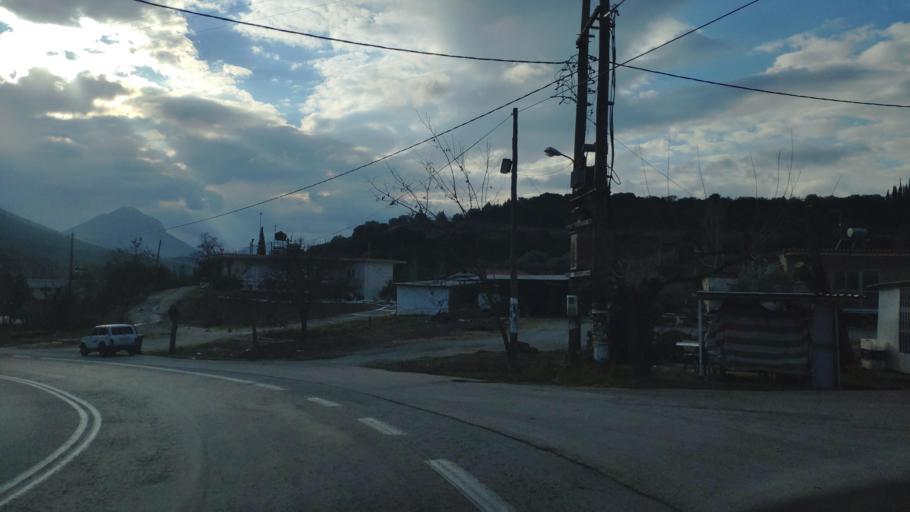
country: GR
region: Peloponnese
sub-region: Nomos Korinthias
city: Nemea
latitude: 37.7826
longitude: 22.7203
